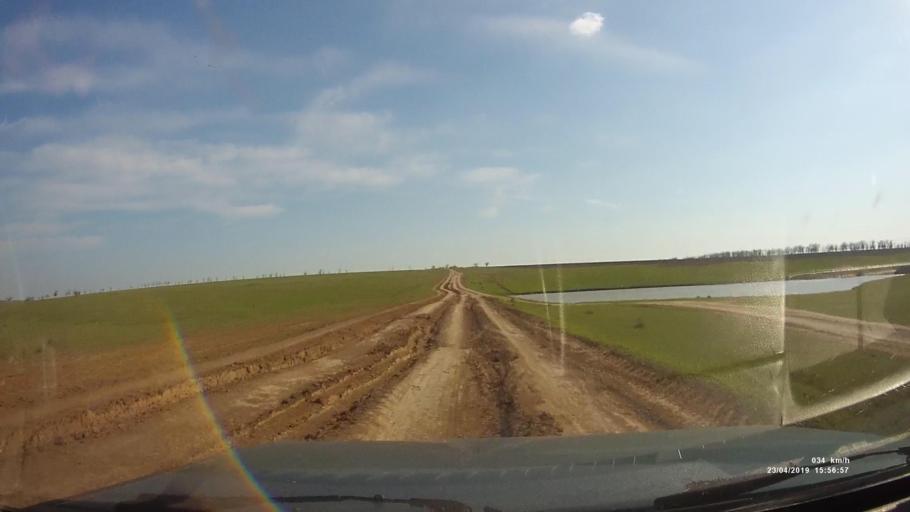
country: RU
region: Rostov
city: Remontnoye
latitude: 46.5345
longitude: 43.1106
